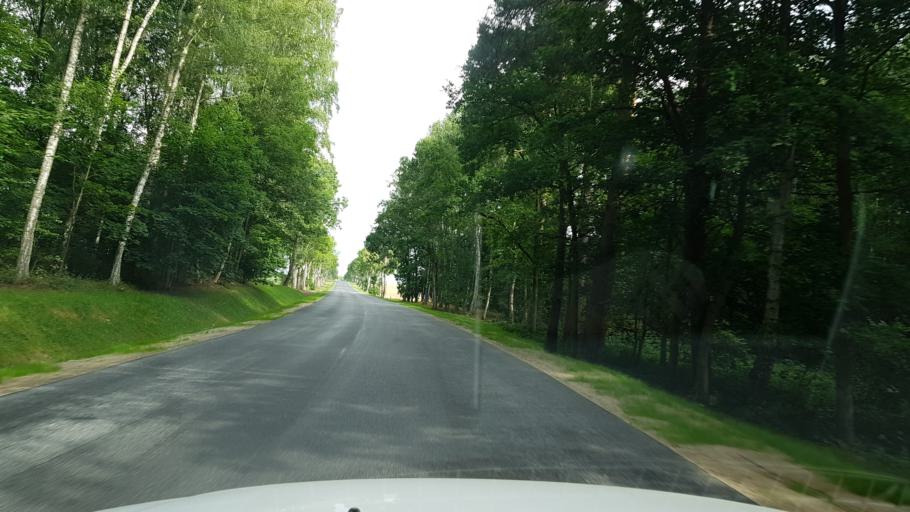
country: PL
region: West Pomeranian Voivodeship
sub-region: Powiat gryficki
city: Gryfice
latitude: 53.8590
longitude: 15.2258
